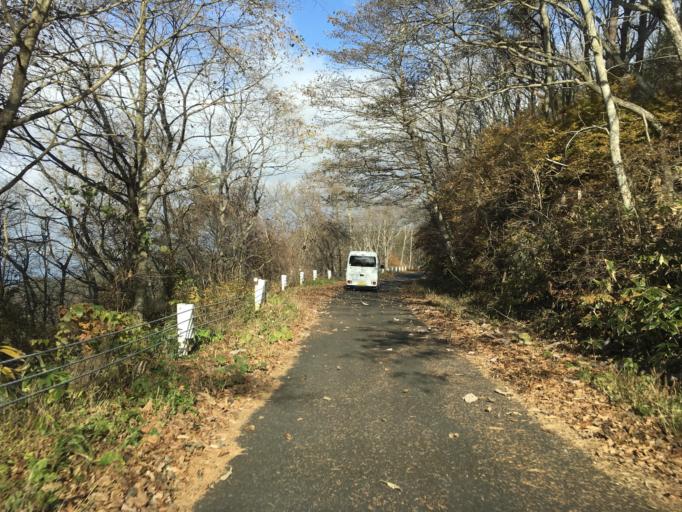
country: JP
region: Iwate
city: Mizusawa
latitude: 39.1275
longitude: 141.3029
